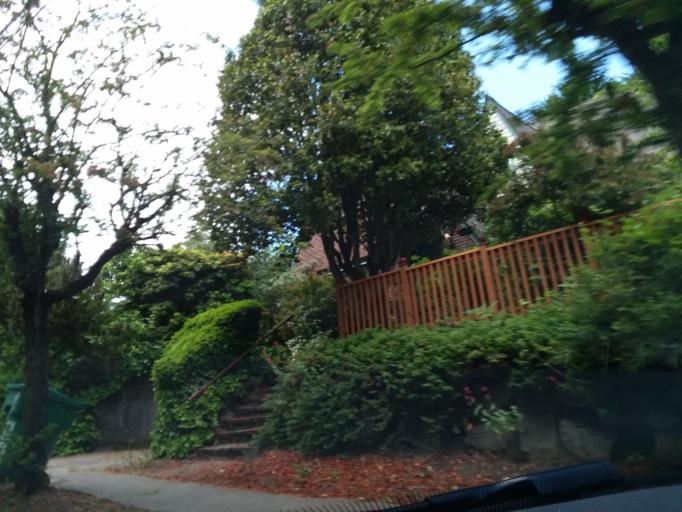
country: US
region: Washington
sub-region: King County
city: Seattle
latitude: 47.6556
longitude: -122.3286
